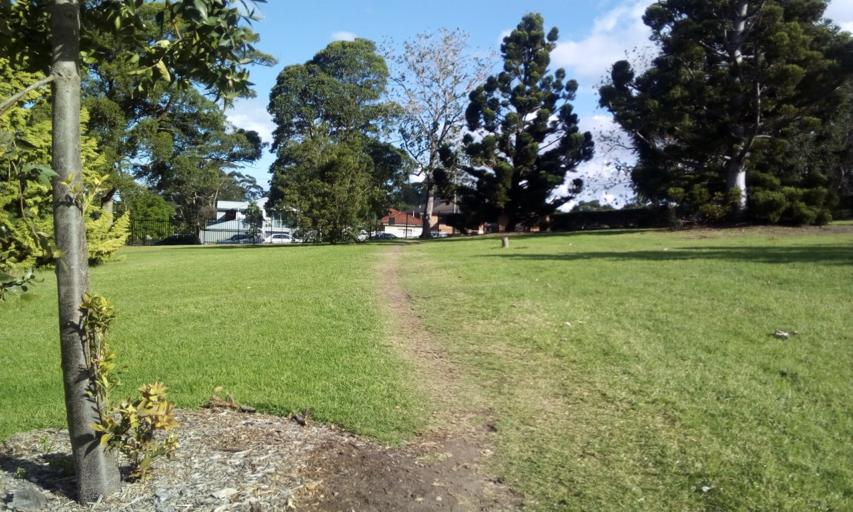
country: AU
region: New South Wales
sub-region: Wollongong
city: Keiraville
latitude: -34.4110
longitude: 150.8741
